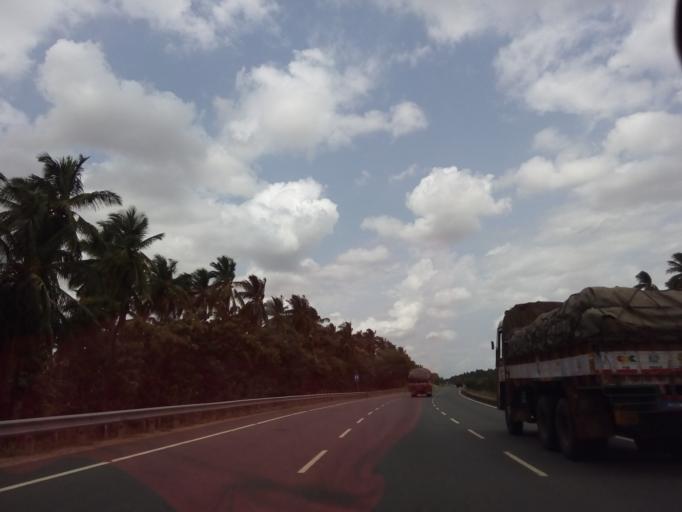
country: IN
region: Karnataka
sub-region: Chitradurga
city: Hiriyur
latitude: 13.9059
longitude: 76.6675
